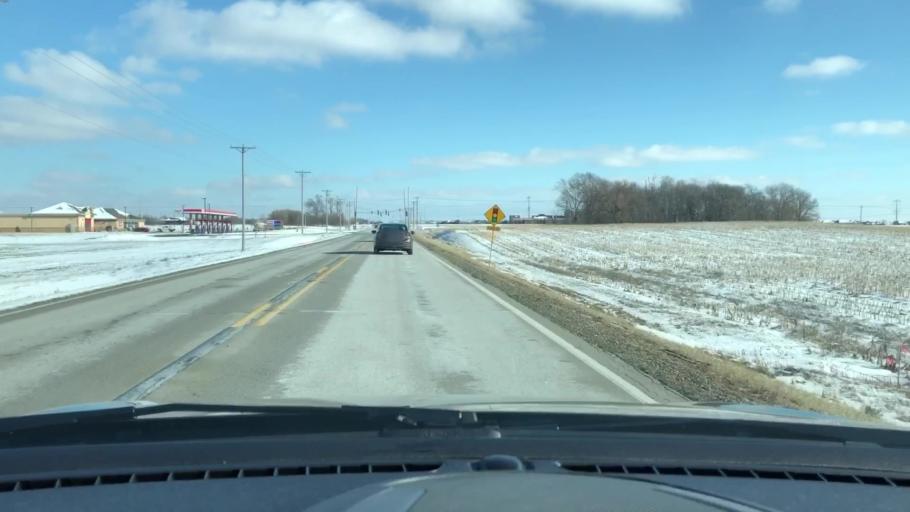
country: US
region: Illinois
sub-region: Will County
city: New Lenox
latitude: 41.4830
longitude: -87.9687
